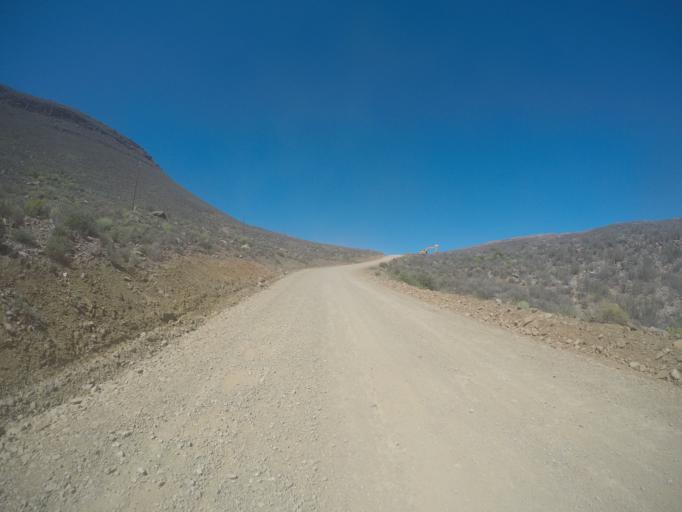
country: ZA
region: Western Cape
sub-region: West Coast District Municipality
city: Clanwilliam
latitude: -32.6054
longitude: 19.3682
